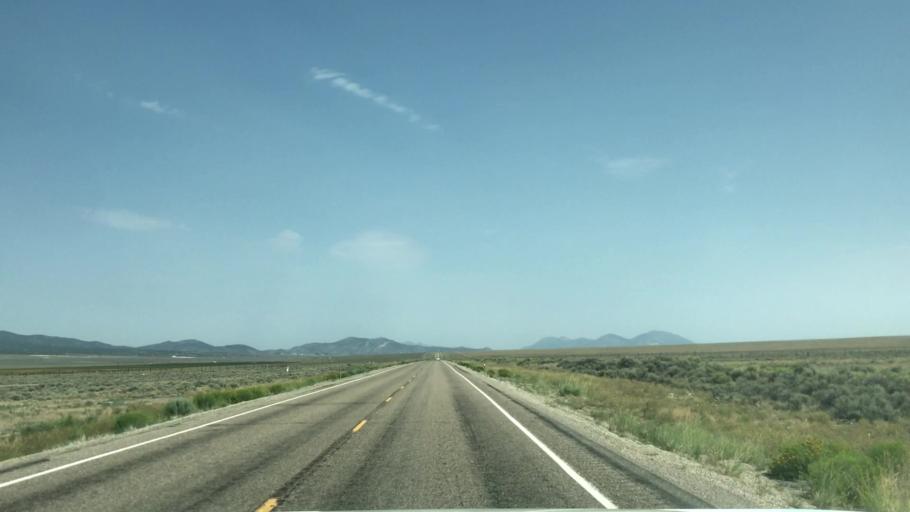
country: US
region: Nevada
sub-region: White Pine County
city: Ely
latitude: 39.1266
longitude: -114.7789
